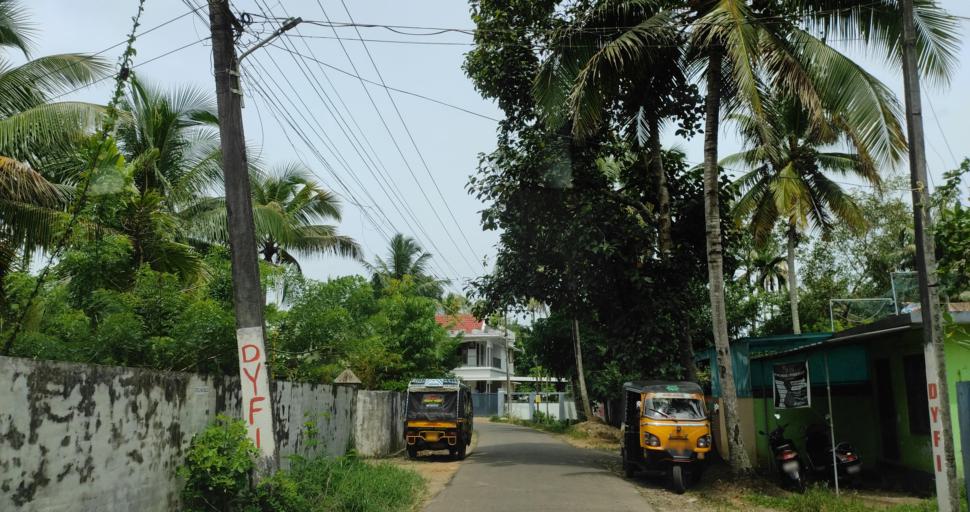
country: IN
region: Kerala
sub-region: Alappuzha
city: Shertallai
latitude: 9.6751
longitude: 76.3567
